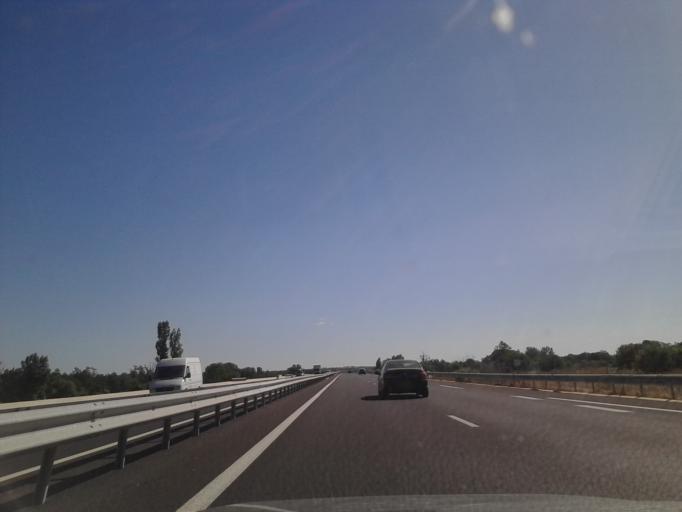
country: FR
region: Languedoc-Roussillon
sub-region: Departement de l'Herault
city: Montblanc
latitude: 43.4008
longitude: 3.3397
